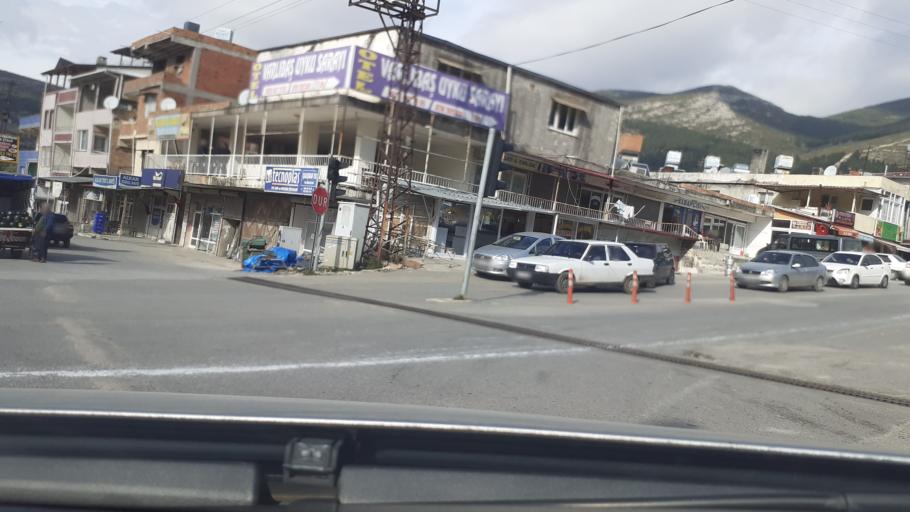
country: TR
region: Hatay
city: Belen
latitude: 36.4879
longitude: 36.2231
